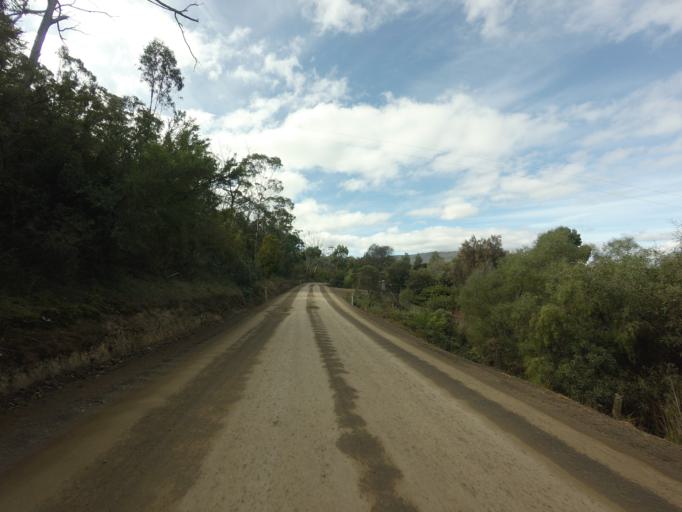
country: AU
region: Tasmania
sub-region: Clarence
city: Sandford
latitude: -43.0936
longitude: 147.7251
